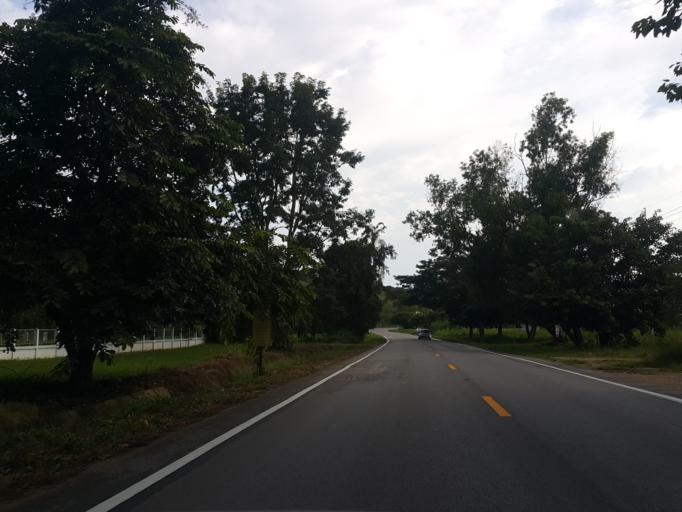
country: TH
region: Chiang Mai
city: Phrao
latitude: 19.2349
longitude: 99.1860
